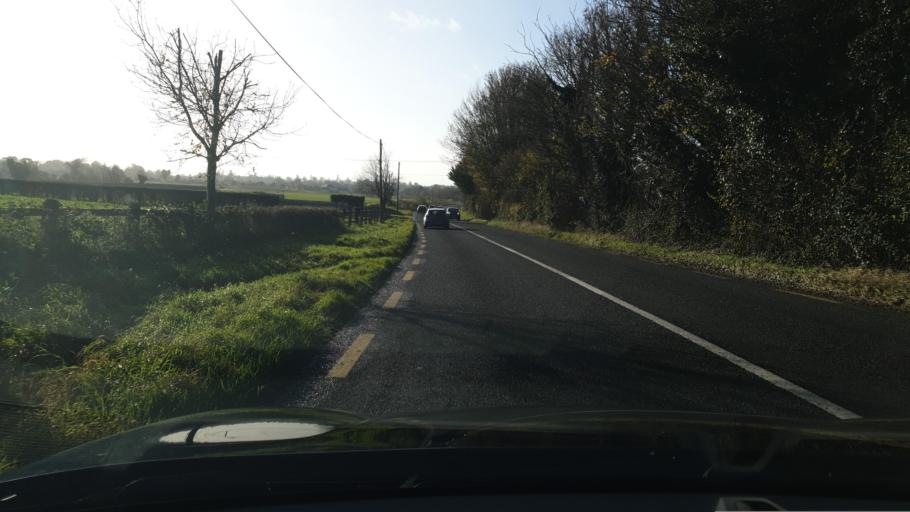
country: IE
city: Confey
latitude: 53.4025
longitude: -6.5288
